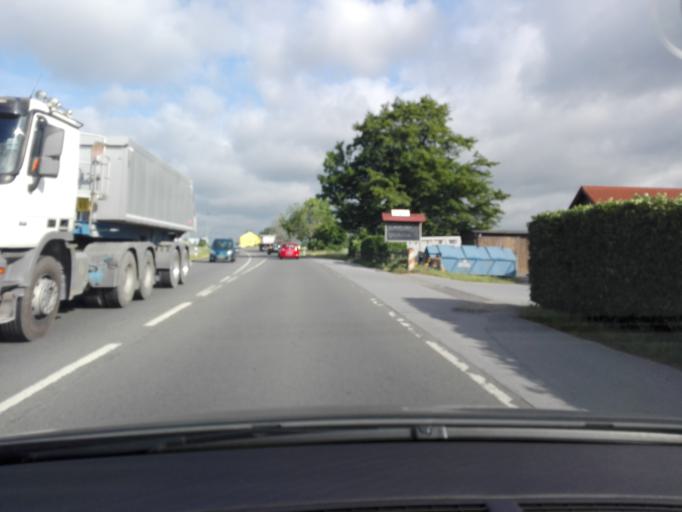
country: DE
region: North Rhine-Westphalia
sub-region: Regierungsbezirk Arnsberg
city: Menden
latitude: 51.4502
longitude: 7.7549
